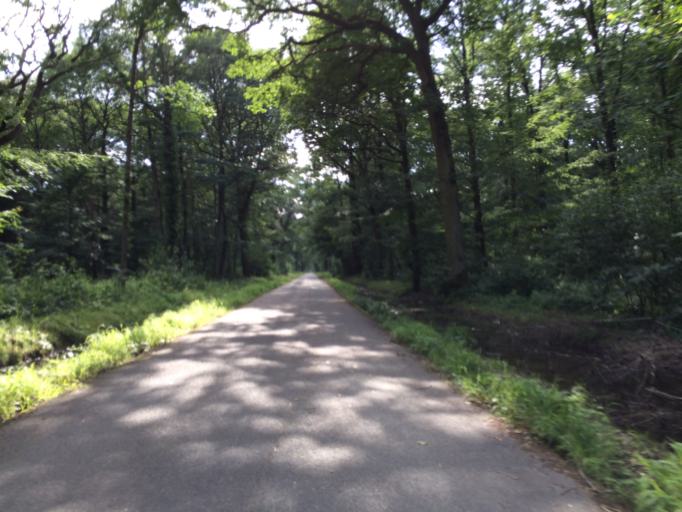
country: FR
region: Ile-de-France
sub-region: Departement de l'Essonne
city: Soisy-sur-Seine
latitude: 48.6618
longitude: 2.4554
